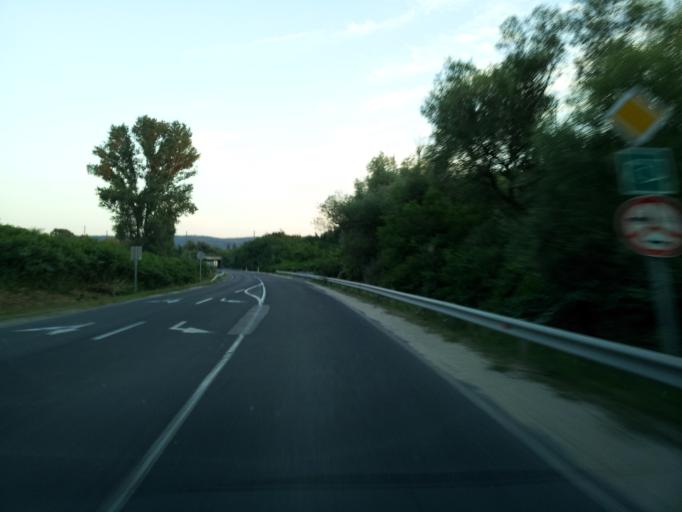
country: HU
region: Komarom-Esztergom
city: Tatabanya
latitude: 47.5551
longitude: 18.4468
